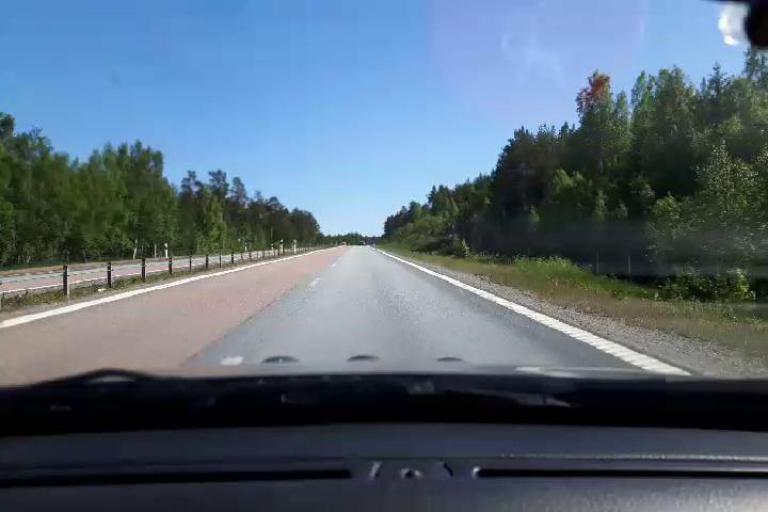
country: SE
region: Gaevleborg
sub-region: Soderhamns Kommun
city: Soderhamn
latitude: 61.3254
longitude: 17.0276
